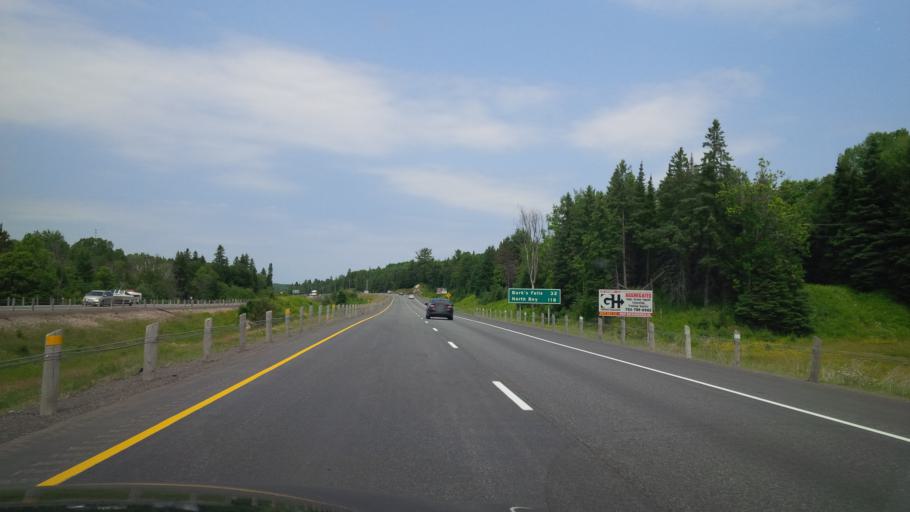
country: CA
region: Ontario
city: Huntsville
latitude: 45.3805
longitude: -79.2233
